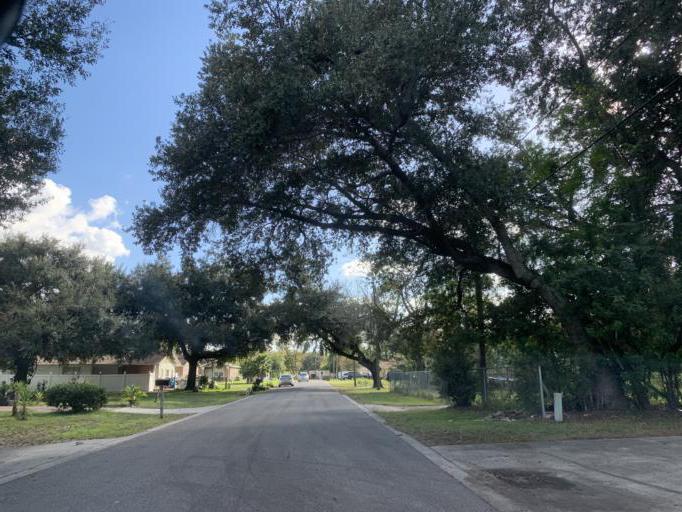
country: US
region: Florida
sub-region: Orange County
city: Eatonville
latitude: 28.6181
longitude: -81.3952
